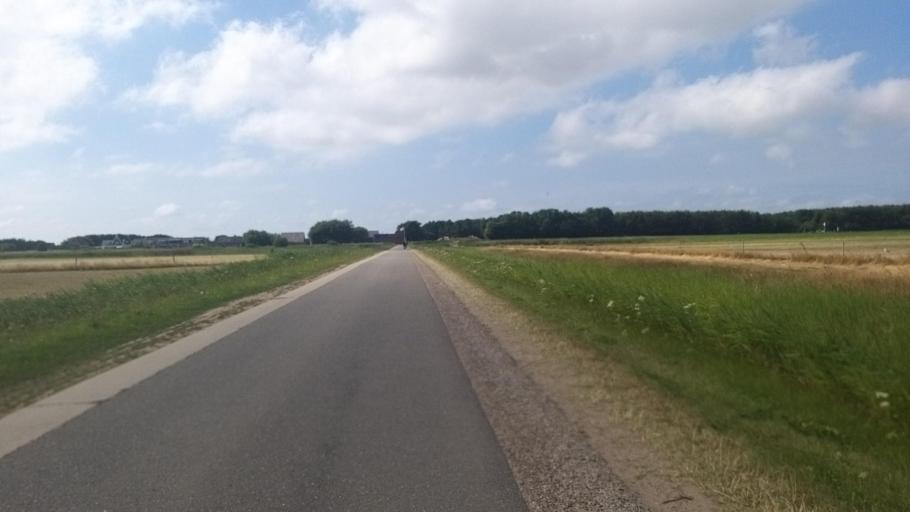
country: NL
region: North Holland
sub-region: Gemeente Texel
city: Den Burg
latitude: 53.1452
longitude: 4.8654
